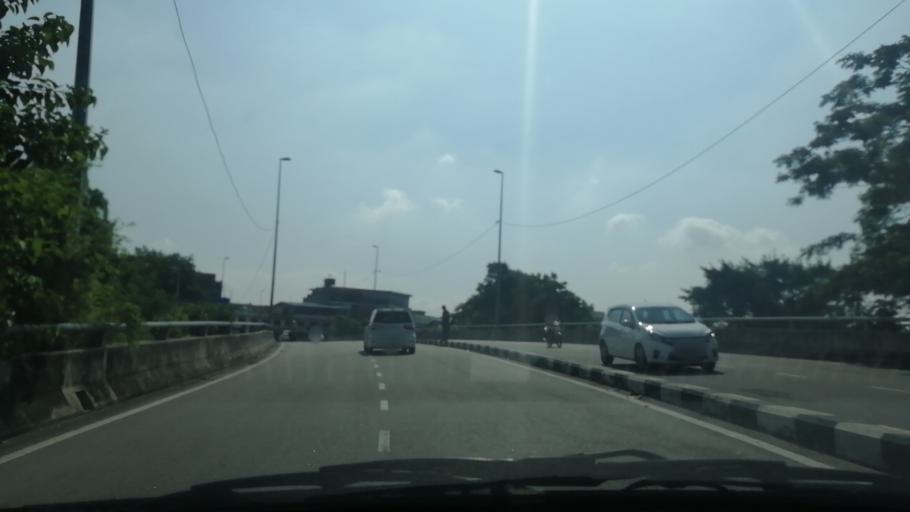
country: MY
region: Kedah
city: Sungai Petani
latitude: 5.6374
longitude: 100.4923
